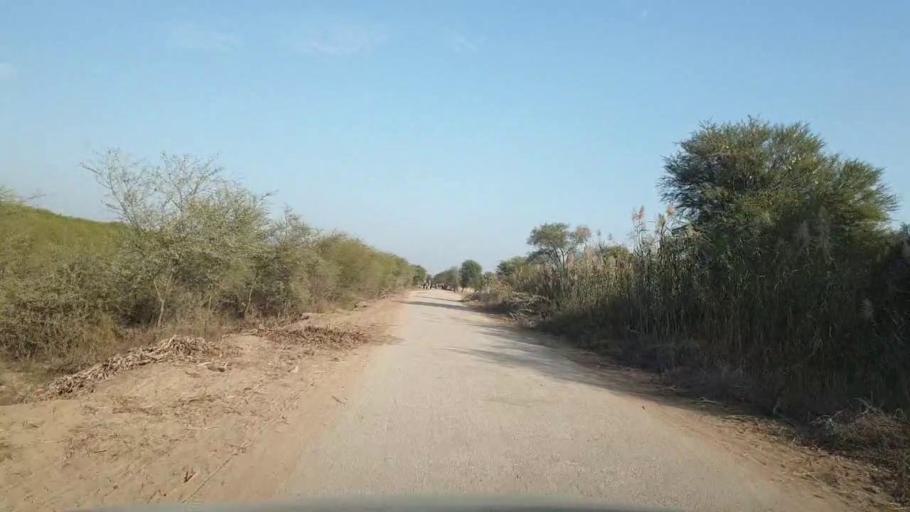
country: PK
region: Sindh
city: Tando Allahyar
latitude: 25.5938
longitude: 68.6744
